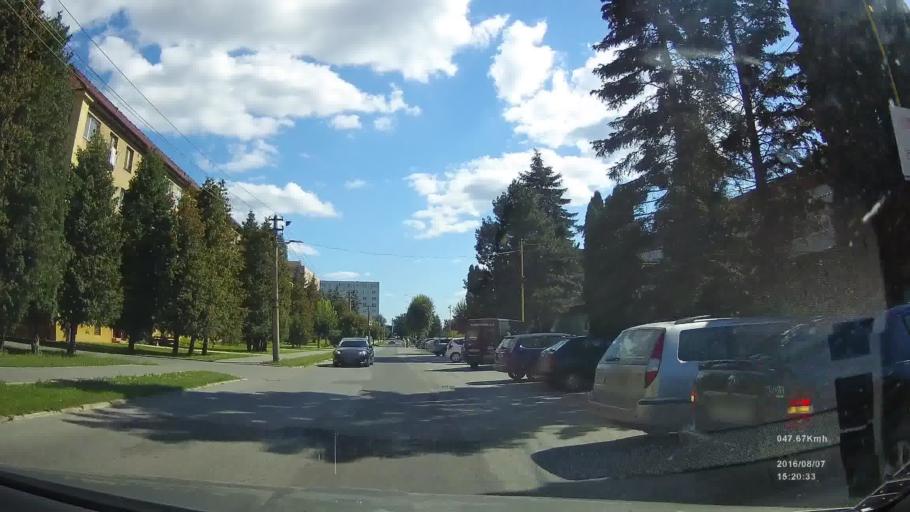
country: SK
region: Presovsky
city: Stropkov
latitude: 49.2013
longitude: 21.6484
